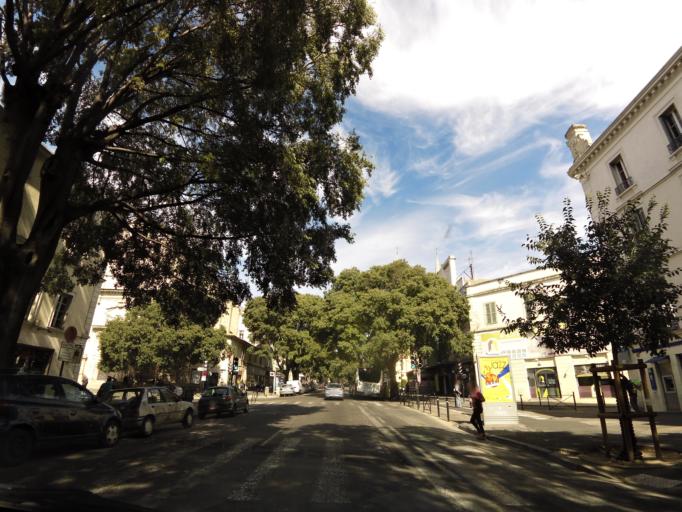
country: FR
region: Languedoc-Roussillon
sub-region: Departement du Gard
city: Nimes
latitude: 43.8382
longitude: 4.3631
